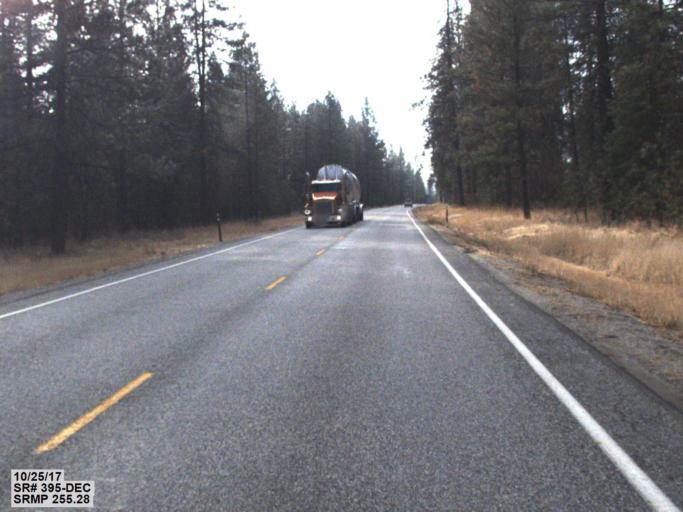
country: US
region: Washington
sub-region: Stevens County
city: Kettle Falls
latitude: 48.8055
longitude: -118.1629
